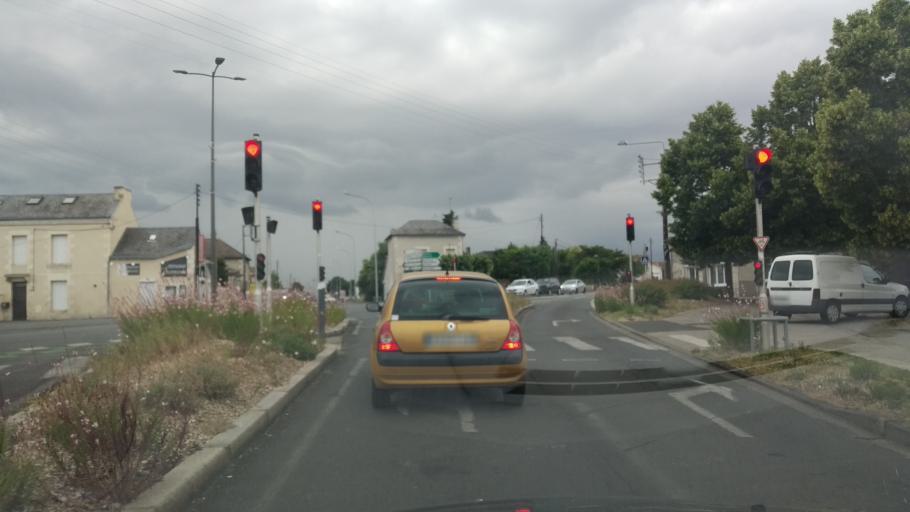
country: FR
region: Poitou-Charentes
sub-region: Departement de la Vienne
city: Poitiers
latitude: 46.5974
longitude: 0.3272
